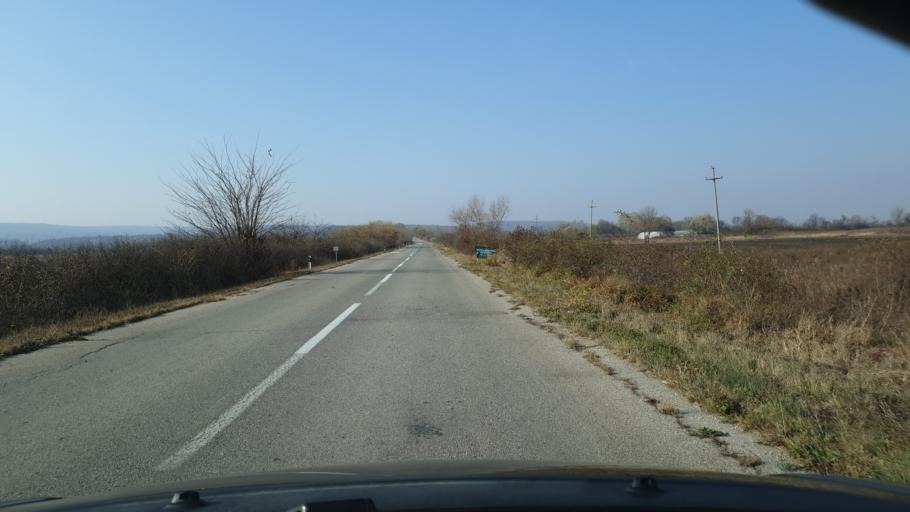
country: BG
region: Vidin
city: Bregovo
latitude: 44.1571
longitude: 22.6126
